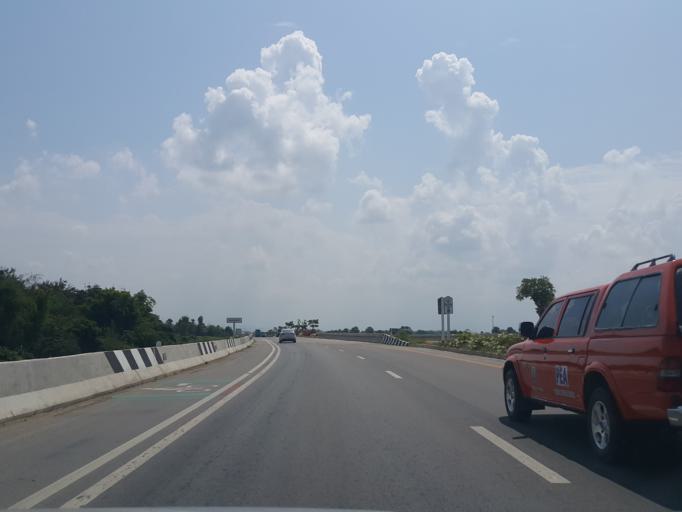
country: TH
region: Chiang Mai
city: Mae Wang
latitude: 18.5957
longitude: 98.8342
